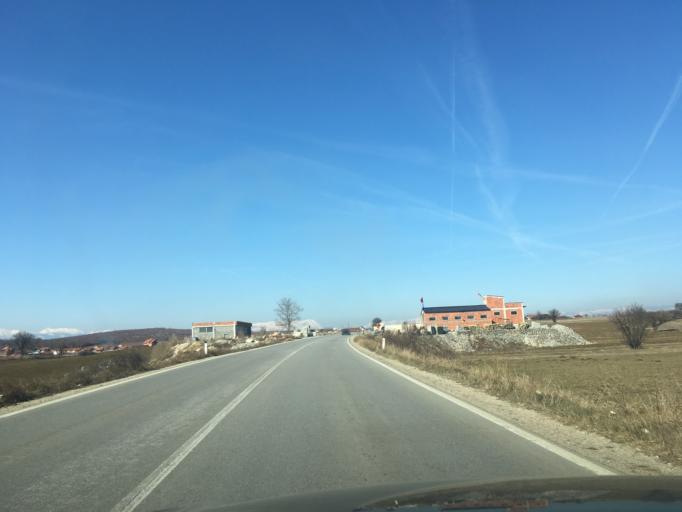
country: XK
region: Prizren
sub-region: Komuna e Malisheves
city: Llazice
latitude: 42.5788
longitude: 20.6987
